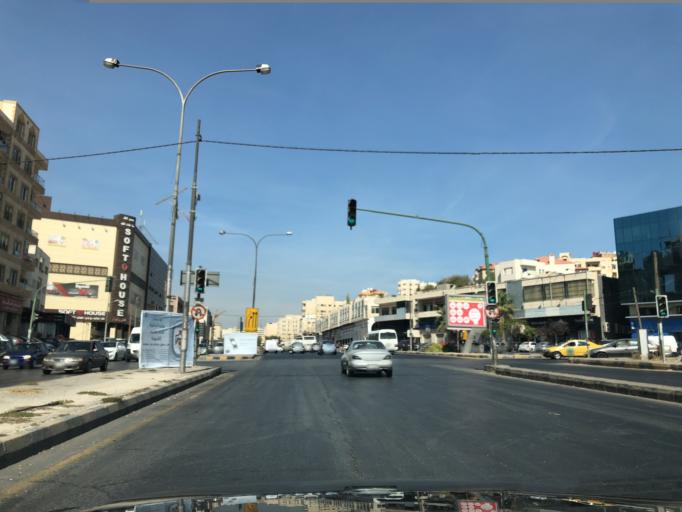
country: JO
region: Amman
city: Al Jubayhah
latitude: 32.0181
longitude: 35.8656
